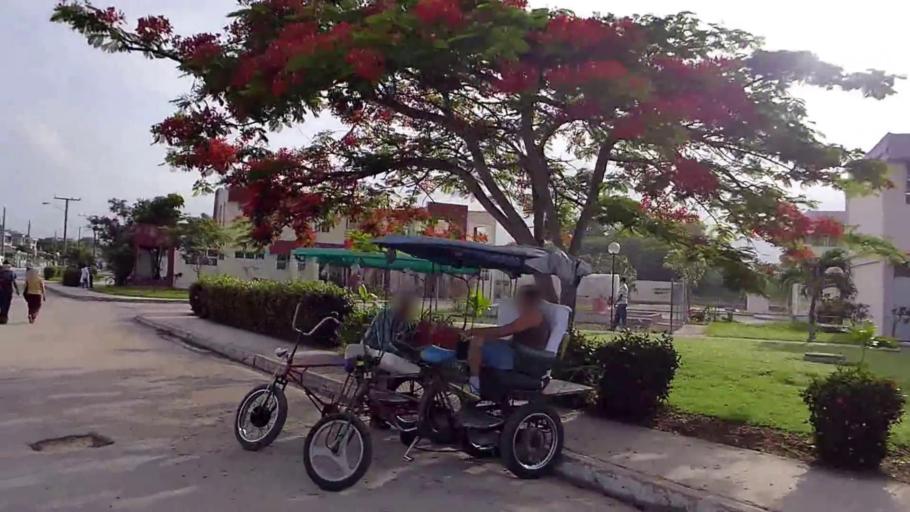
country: CU
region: Camaguey
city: Camaguey
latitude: 21.3833
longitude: -77.9360
